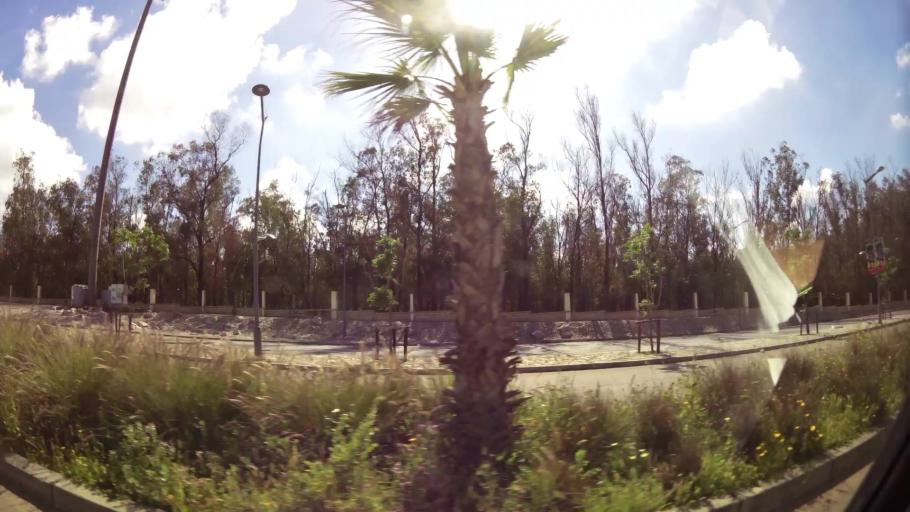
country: MA
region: Grand Casablanca
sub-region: Nouaceur
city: Bouskoura
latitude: 33.4769
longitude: -7.6207
